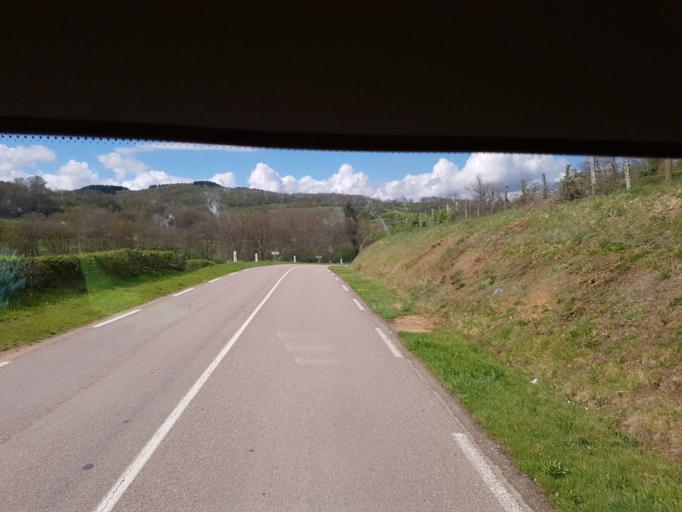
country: FR
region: Bourgogne
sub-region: Departement de Saone-et-Loire
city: Autun
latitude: 47.0971
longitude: 4.2327
